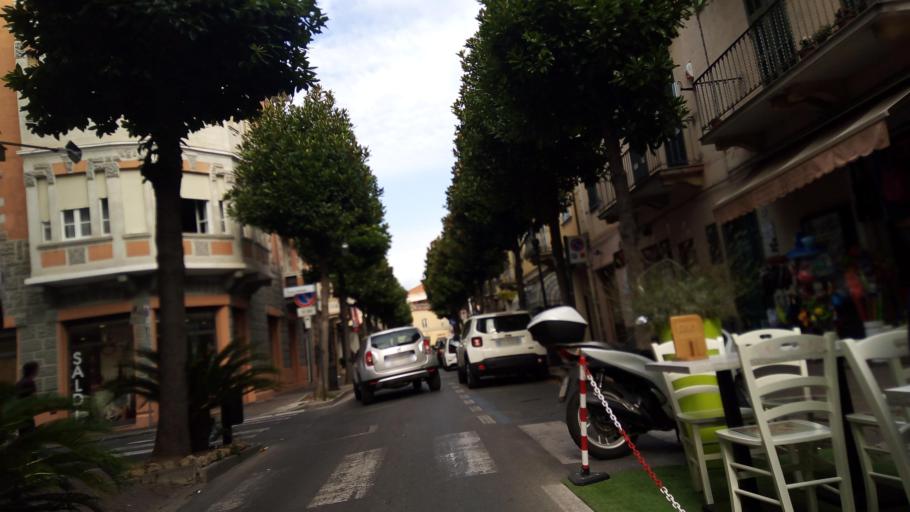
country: IT
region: Liguria
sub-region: Provincia di Savona
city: Albenga
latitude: 44.0487
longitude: 8.2167
